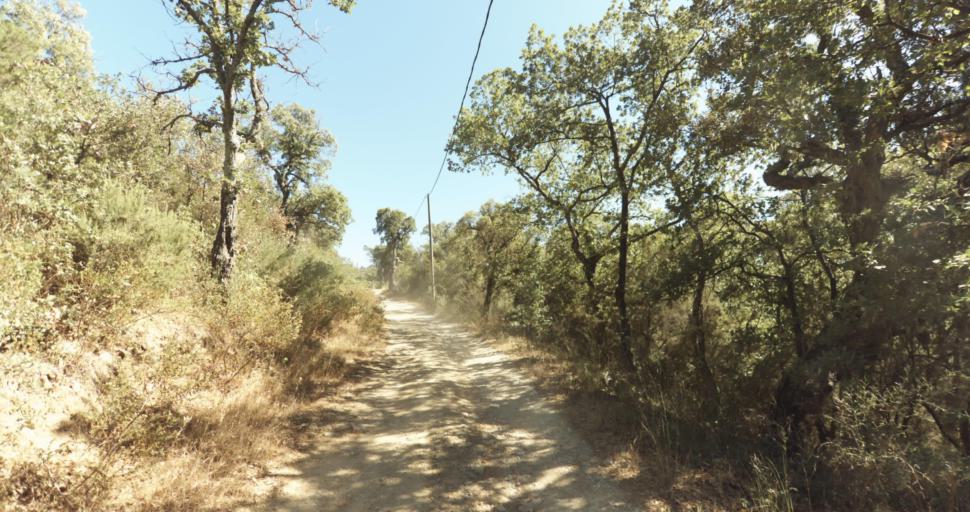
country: FR
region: Provence-Alpes-Cote d'Azur
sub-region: Departement du Var
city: Gassin
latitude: 43.2403
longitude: 6.5841
